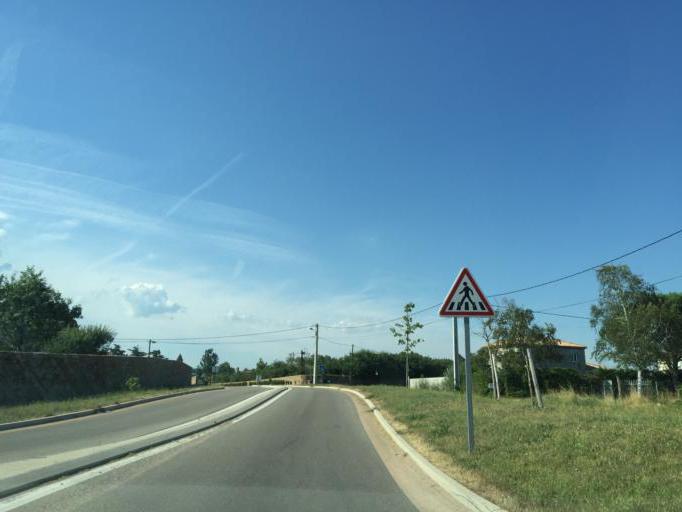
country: FR
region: Rhone-Alpes
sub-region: Departement de l'Ardeche
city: Quintenas
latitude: 45.1877
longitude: 4.6900
